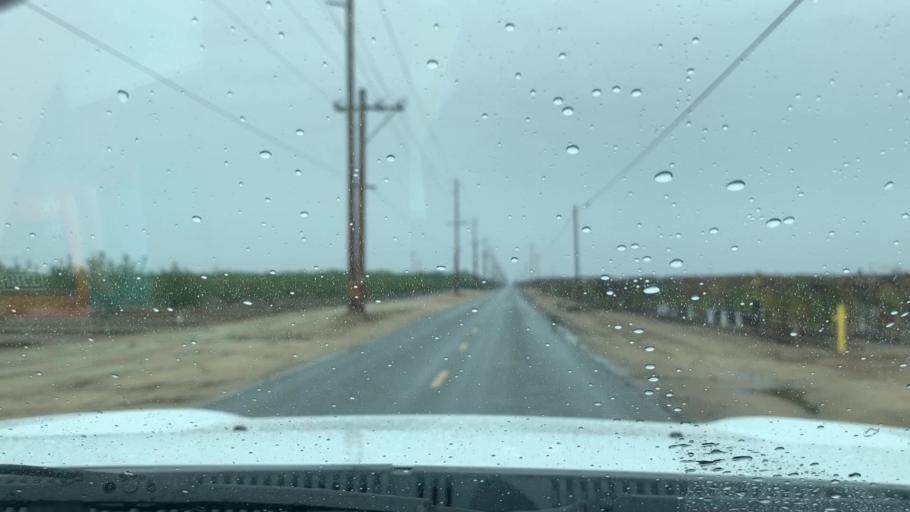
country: US
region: California
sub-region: Kern County
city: Delano
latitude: 35.8340
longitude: -119.2079
